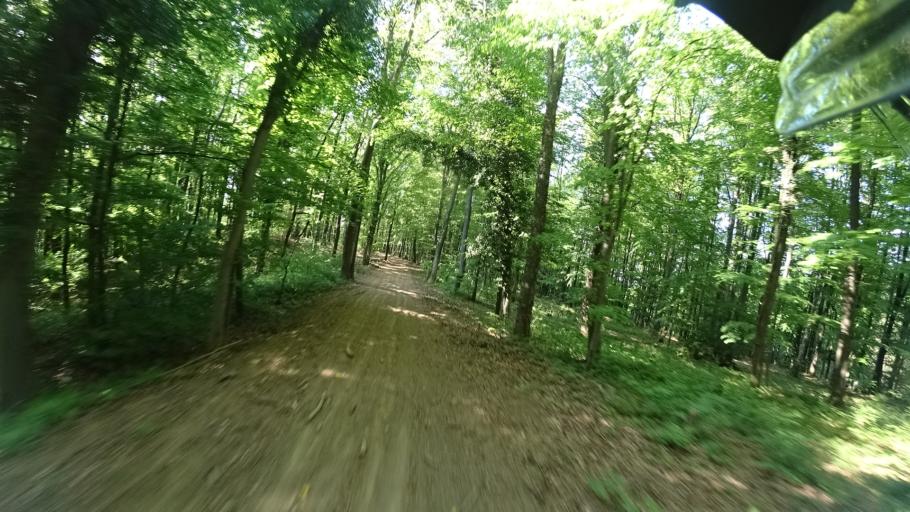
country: HR
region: Zagrebacka
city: Jablanovec
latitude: 45.8985
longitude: 15.9001
